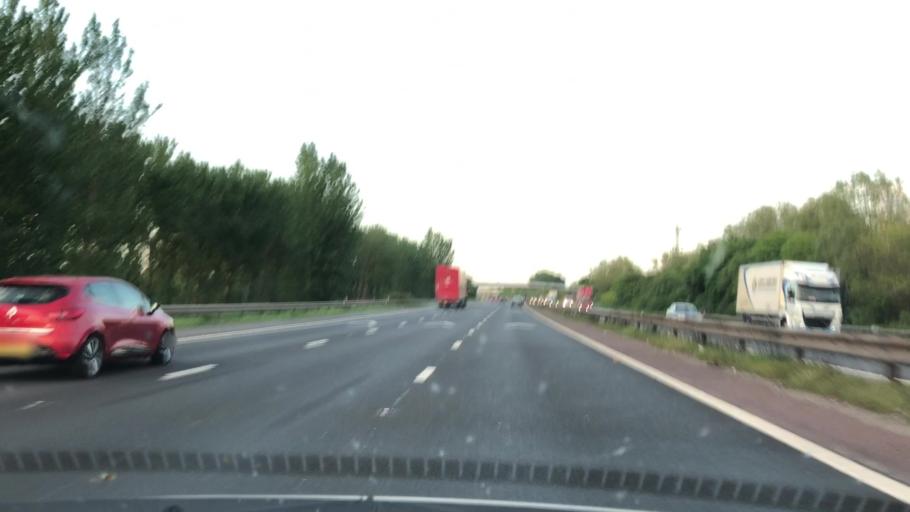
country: GB
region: England
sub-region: Cheshire West and Chester
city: Helsby
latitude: 53.2765
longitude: -2.7775
